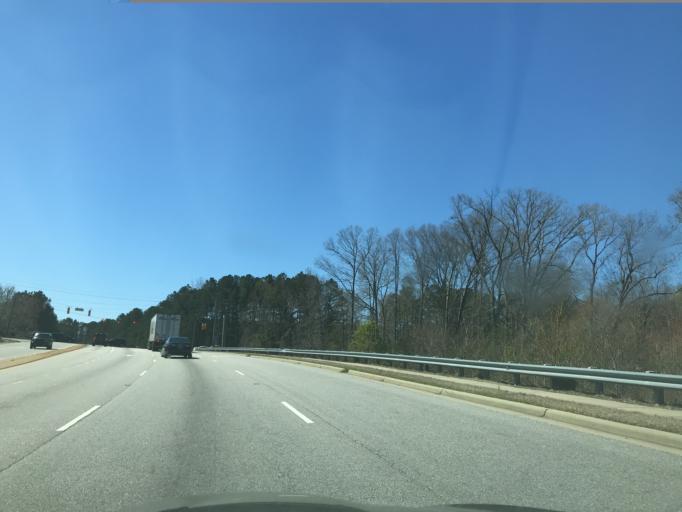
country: US
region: North Carolina
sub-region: Wake County
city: Raleigh
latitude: 35.7437
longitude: -78.6403
